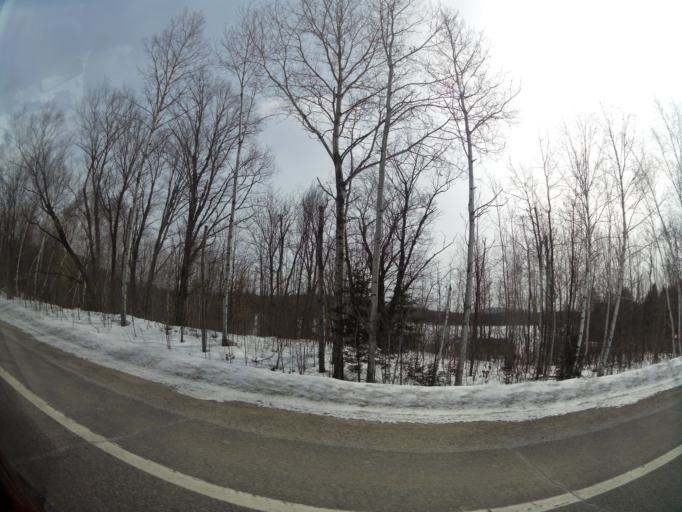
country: CA
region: Quebec
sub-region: Laurentides
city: Mont-Laurier
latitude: 46.3263
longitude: -75.5417
